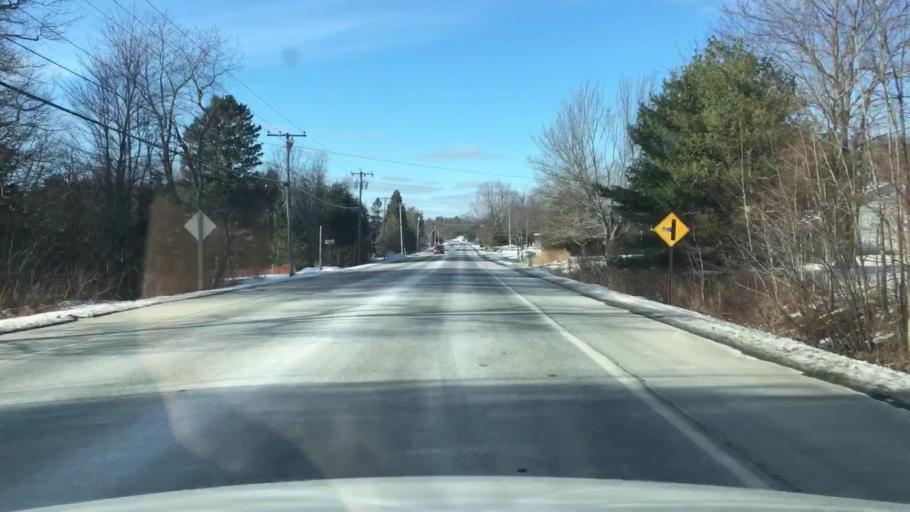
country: US
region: Maine
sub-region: Penobscot County
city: Holden
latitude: 44.7971
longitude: -68.5927
